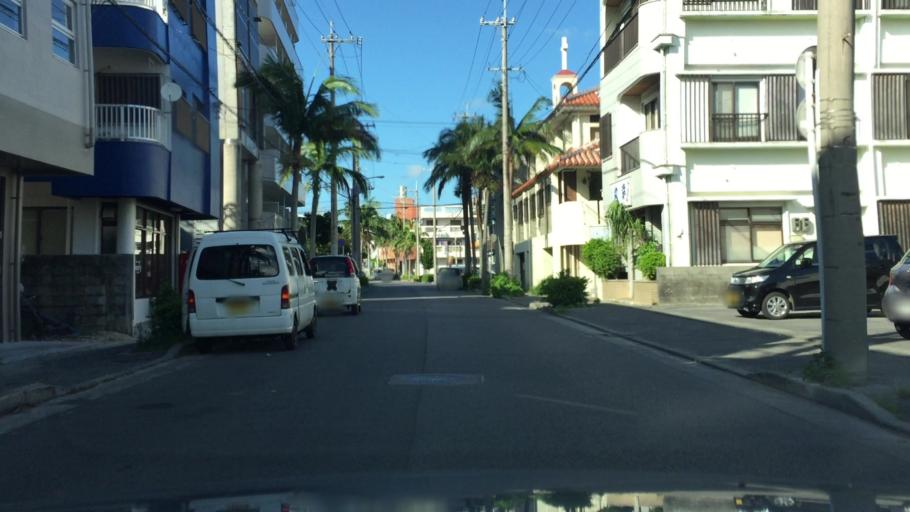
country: JP
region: Okinawa
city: Ishigaki
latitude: 24.3417
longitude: 124.1579
